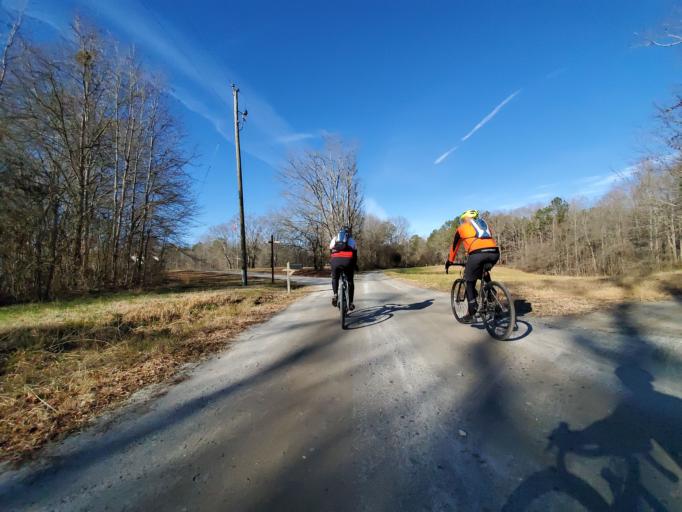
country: US
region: Georgia
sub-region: Fulton County
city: Chattahoochee Hills
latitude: 33.5521
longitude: -84.7985
